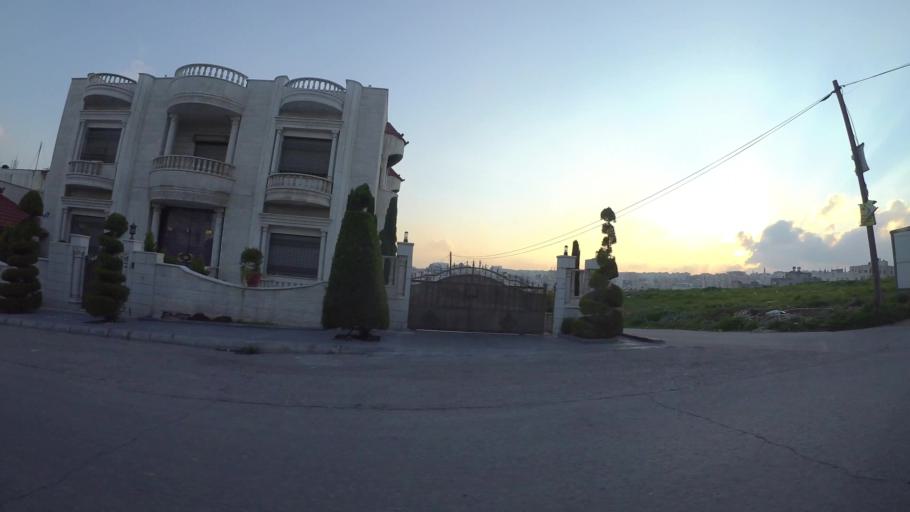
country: JO
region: Amman
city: Amman
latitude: 31.9935
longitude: 35.9494
